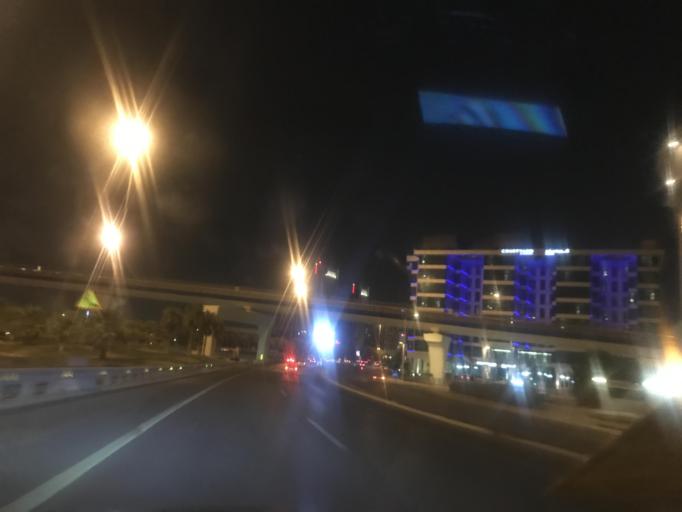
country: SA
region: Ar Riyad
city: Riyadh
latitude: 24.7603
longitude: 46.6501
